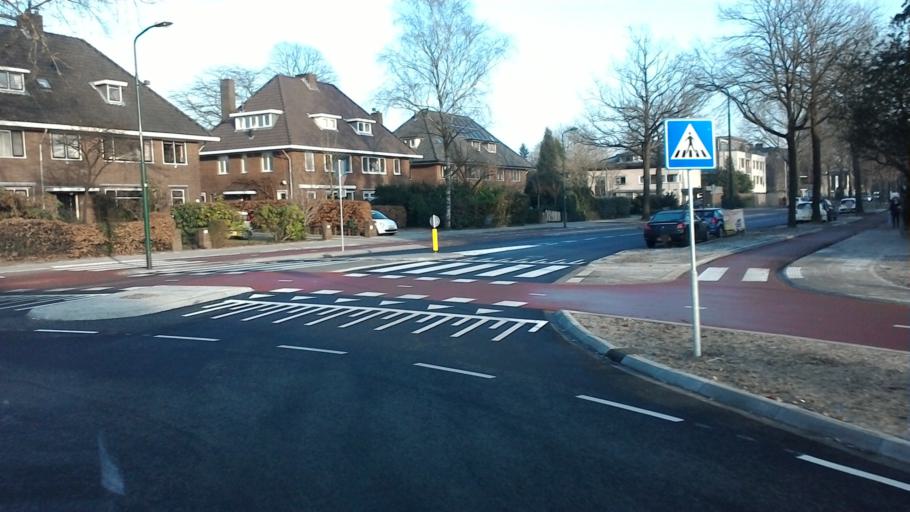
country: NL
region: Utrecht
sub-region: Gemeente De Bilt
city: De Bilt
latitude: 52.1262
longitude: 5.1955
